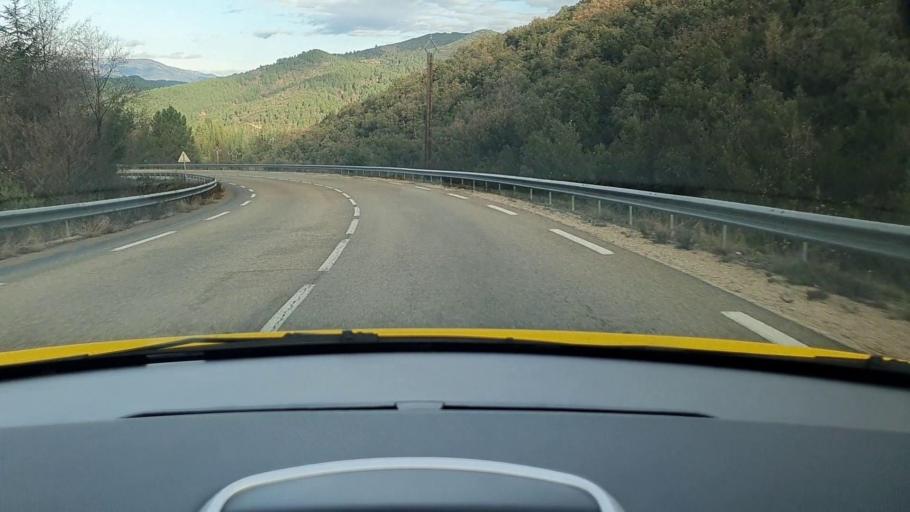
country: FR
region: Languedoc-Roussillon
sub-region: Departement du Gard
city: Laval-Pradel
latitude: 44.2159
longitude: 4.0887
